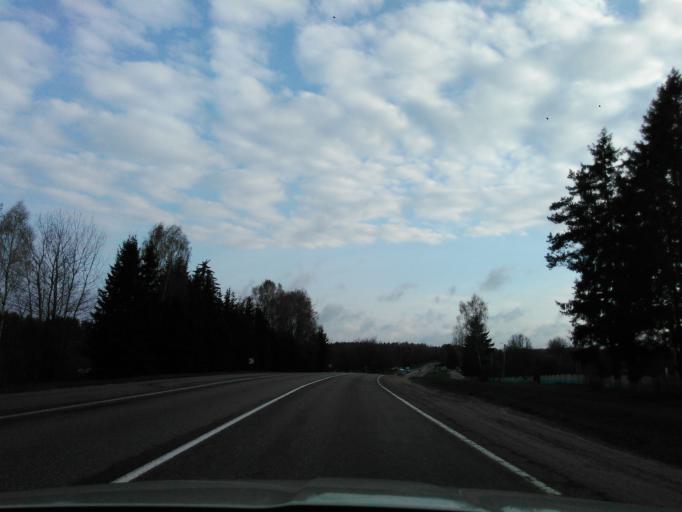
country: BY
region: Minsk
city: Lahoysk
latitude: 54.2939
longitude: 27.8736
